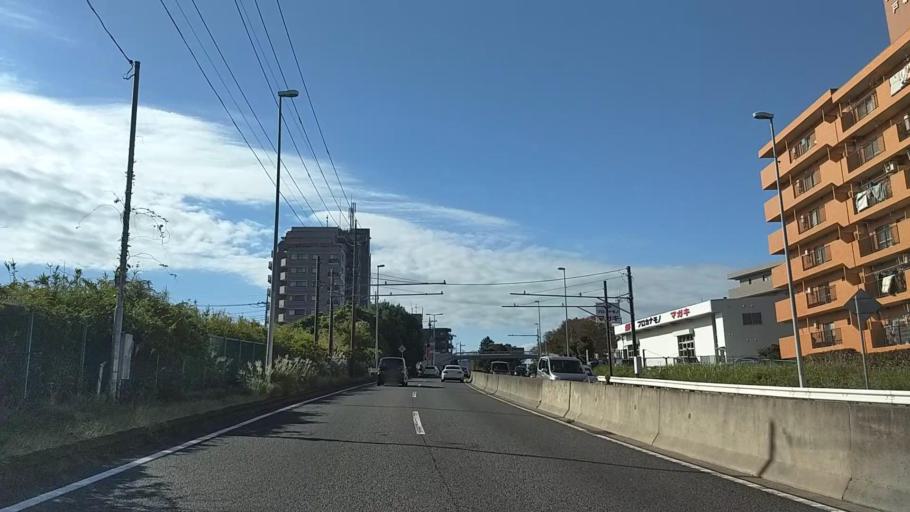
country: JP
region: Kanagawa
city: Fujisawa
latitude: 35.3890
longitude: 139.5202
